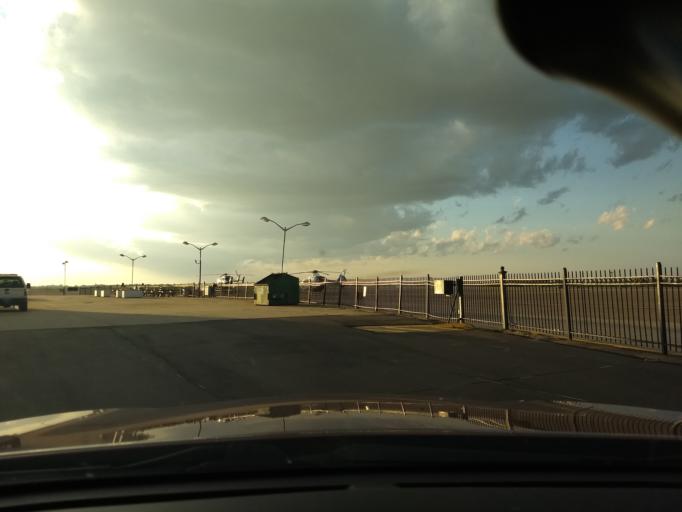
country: US
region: Pennsylvania
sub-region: Allegheny County
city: Pleasant Hills
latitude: 40.3525
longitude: -79.9264
